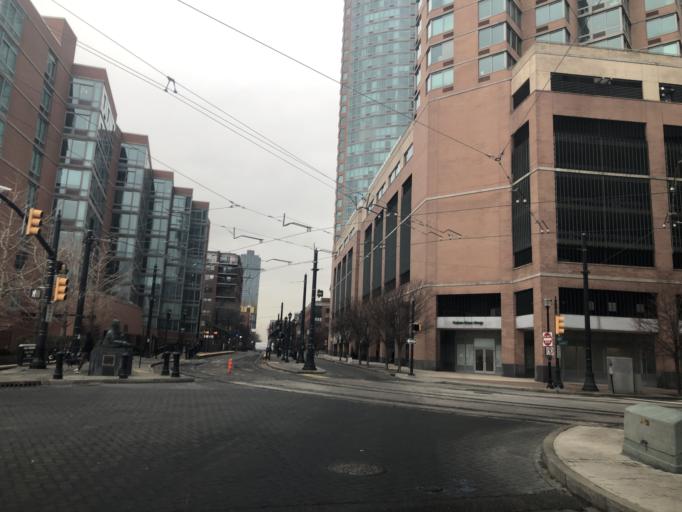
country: US
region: New York
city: New York City
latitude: 40.7128
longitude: -74.0346
